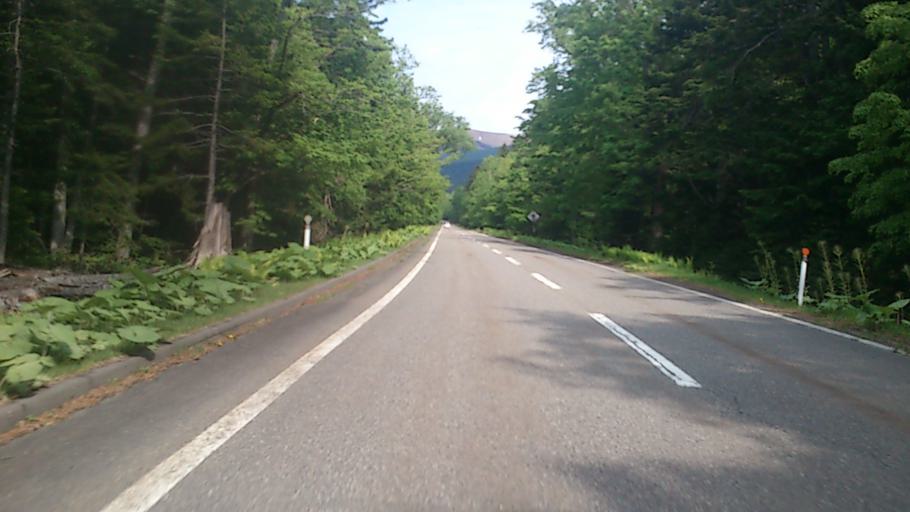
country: JP
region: Hokkaido
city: Kitami
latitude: 43.4024
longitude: 143.9677
